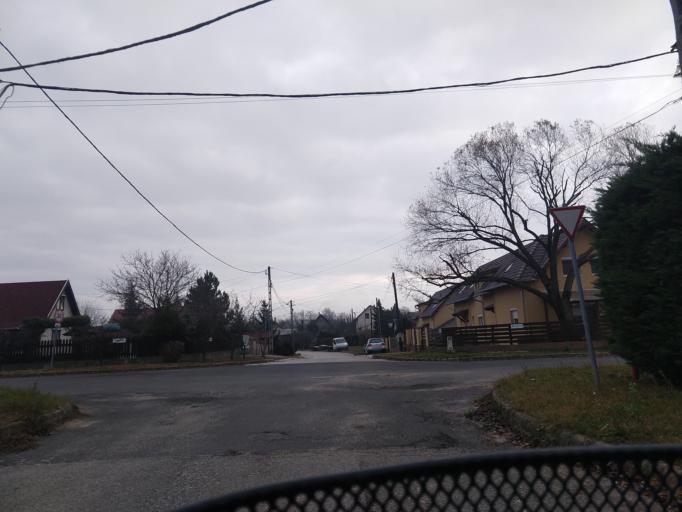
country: HU
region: Pest
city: Orbottyan
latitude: 47.6714
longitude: 19.2880
